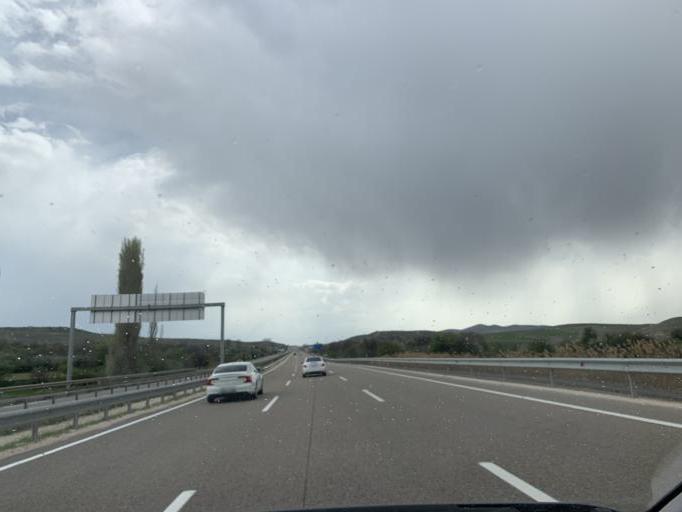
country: TR
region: Eskisehir
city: Sivrihisar
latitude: 39.5254
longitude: 31.6242
